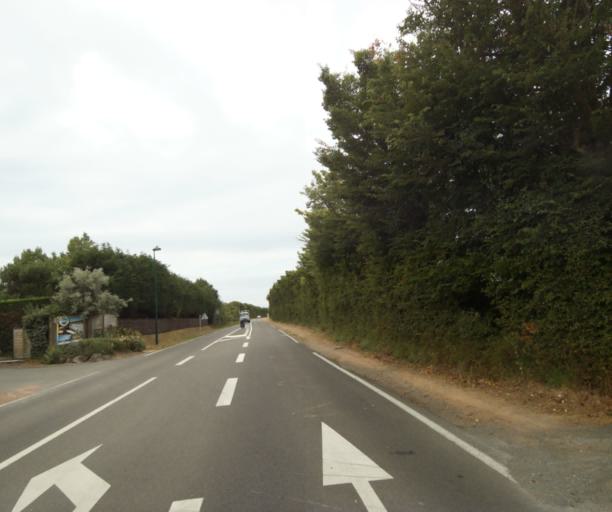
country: FR
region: Pays de la Loire
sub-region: Departement de la Vendee
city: Chateau-d'Olonne
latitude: 46.4740
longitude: -1.7213
